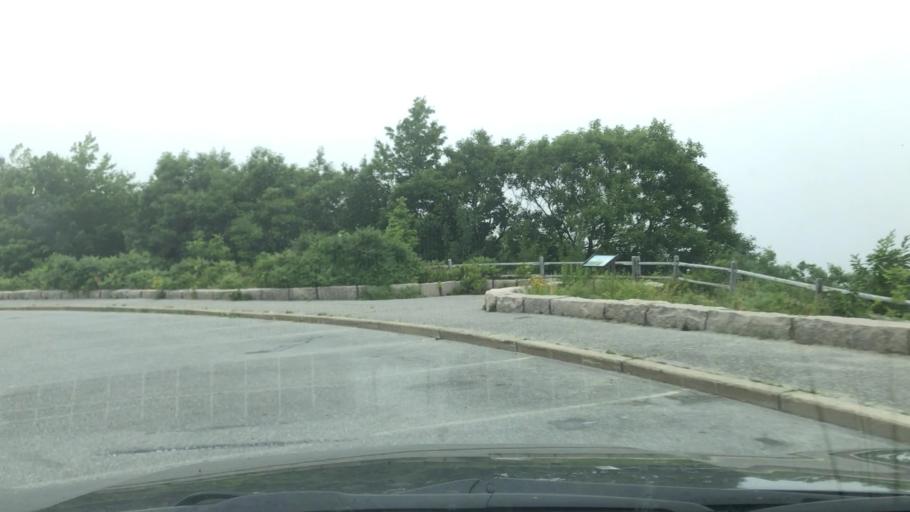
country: US
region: Maine
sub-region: Hancock County
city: Bar Harbor
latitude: 44.3395
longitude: -68.1774
